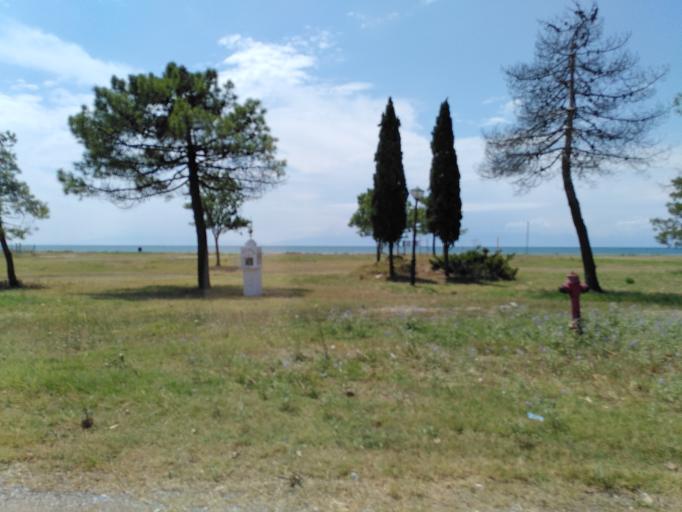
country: GR
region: Central Macedonia
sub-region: Nomos Thessalonikis
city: Nea Michaniona
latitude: 40.4317
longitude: 22.8694
